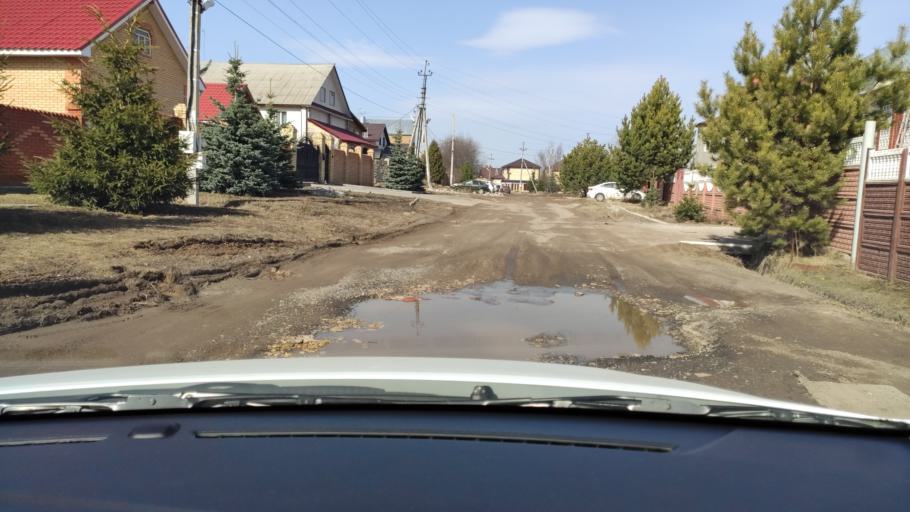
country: RU
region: Tatarstan
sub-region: Gorod Kazan'
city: Kazan
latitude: 55.7858
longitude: 49.2476
